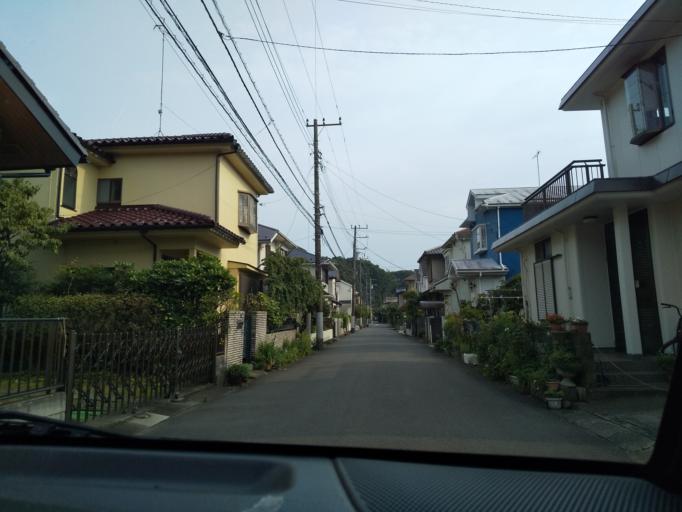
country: JP
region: Kanagawa
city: Zama
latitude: 35.4762
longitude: 139.3971
